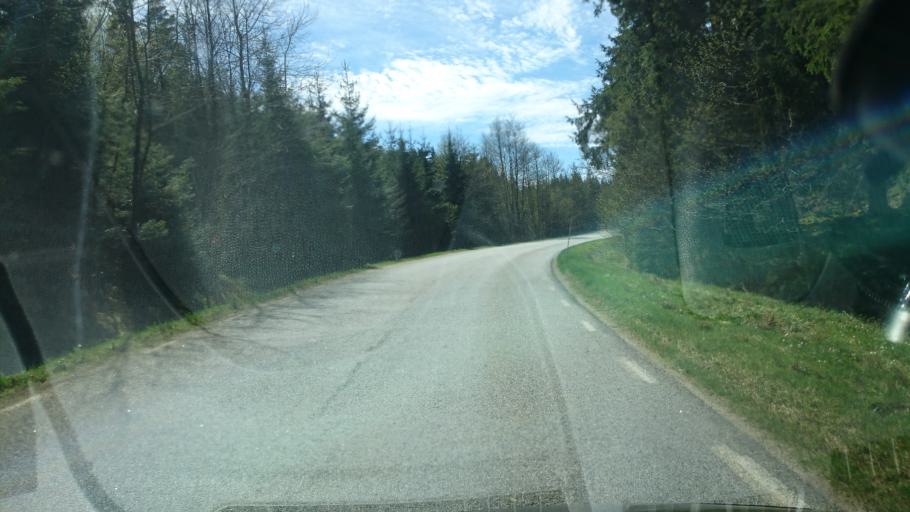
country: SE
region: Vaestra Goetaland
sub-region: Munkedals Kommun
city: Munkedal
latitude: 58.4081
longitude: 11.6727
